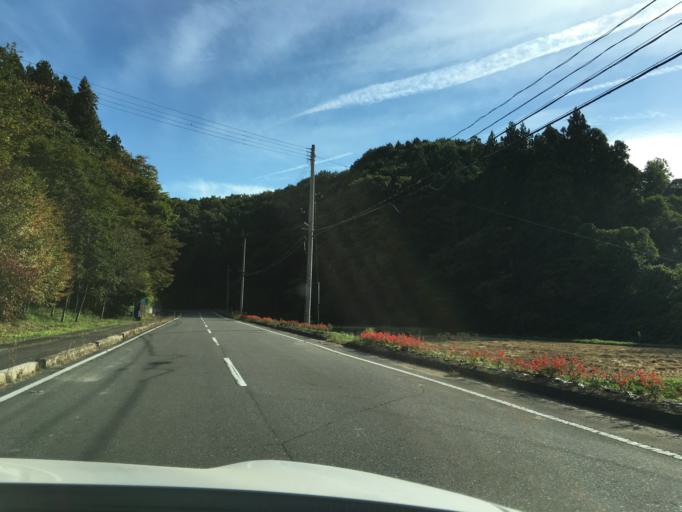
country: JP
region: Fukushima
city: Miharu
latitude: 37.3300
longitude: 140.4914
